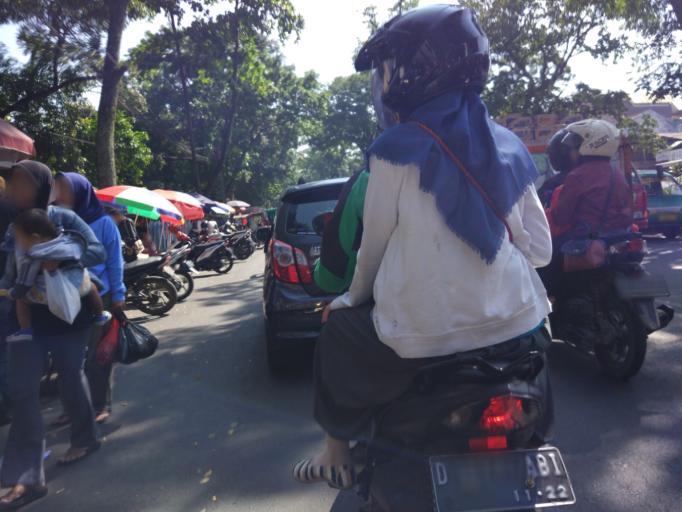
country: ID
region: West Java
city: Bandung
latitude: -6.9367
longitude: 107.6062
